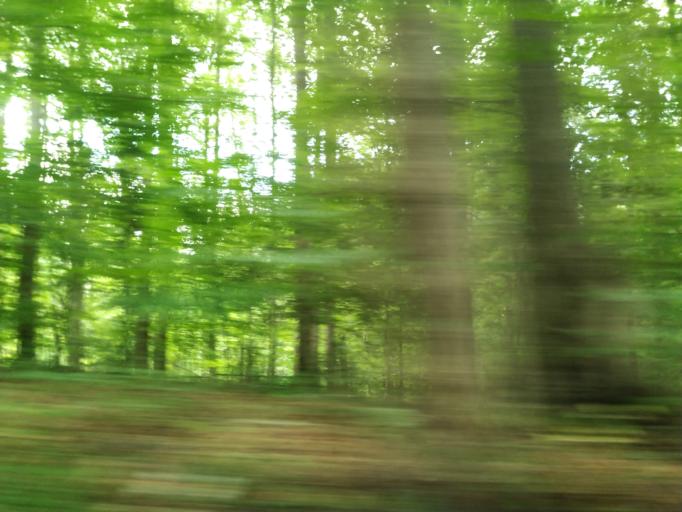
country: US
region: Maryland
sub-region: Anne Arundel County
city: Deale
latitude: 38.8296
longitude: -76.5869
